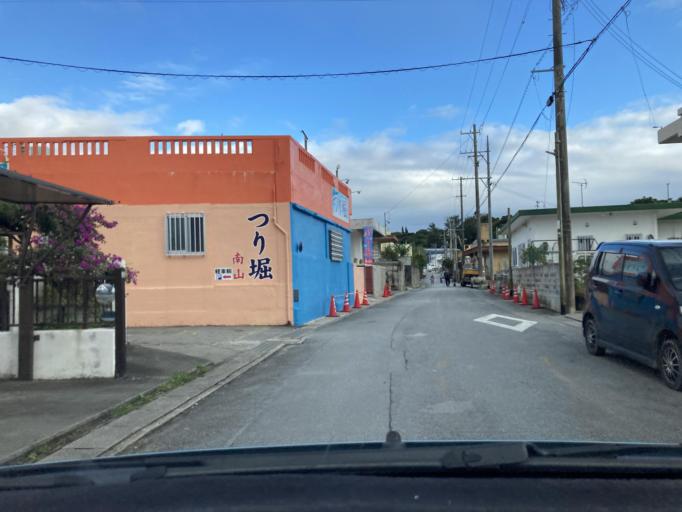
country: JP
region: Okinawa
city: Itoman
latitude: 26.1272
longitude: 127.6922
